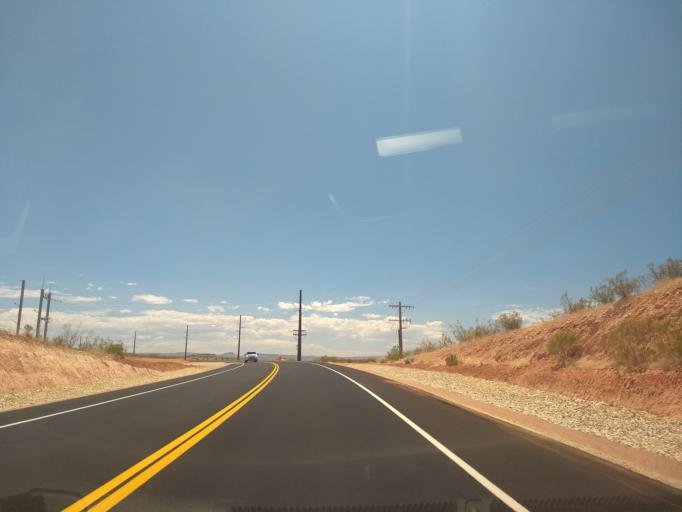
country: US
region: Utah
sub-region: Washington County
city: Washington
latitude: 37.1514
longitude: -113.5178
